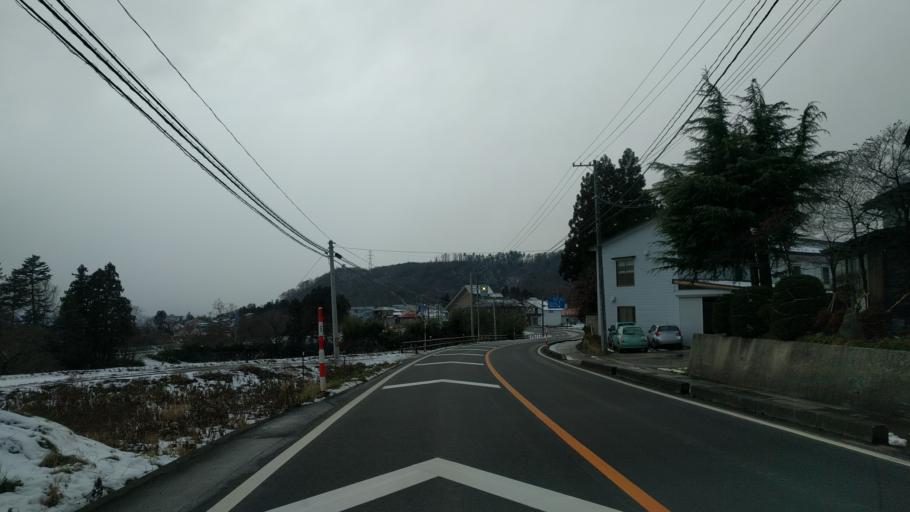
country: JP
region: Fukushima
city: Kitakata
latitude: 37.5762
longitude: 139.9497
